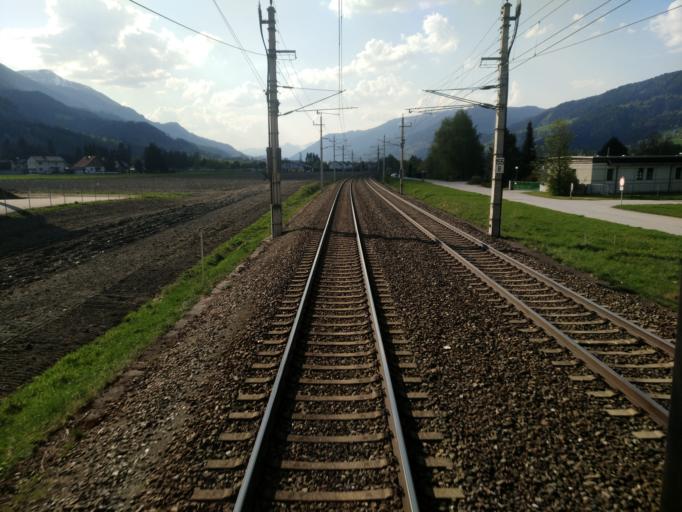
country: AT
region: Styria
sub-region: Politischer Bezirk Liezen
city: Trieben
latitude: 47.4913
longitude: 14.4833
